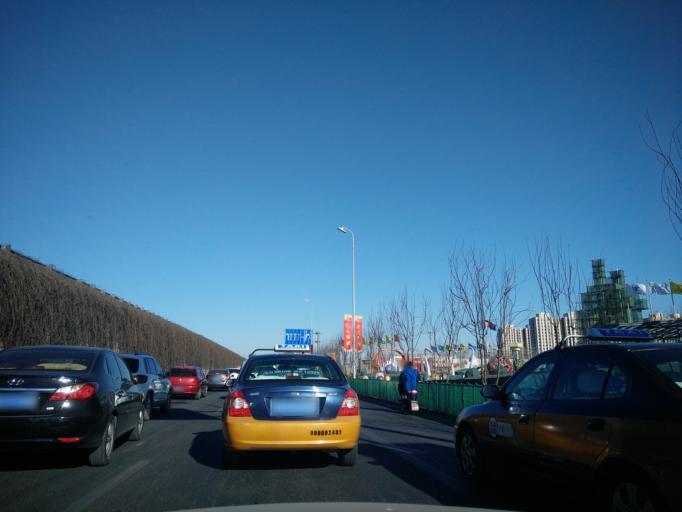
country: CN
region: Beijing
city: Daxing
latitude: 39.7599
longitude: 116.3373
